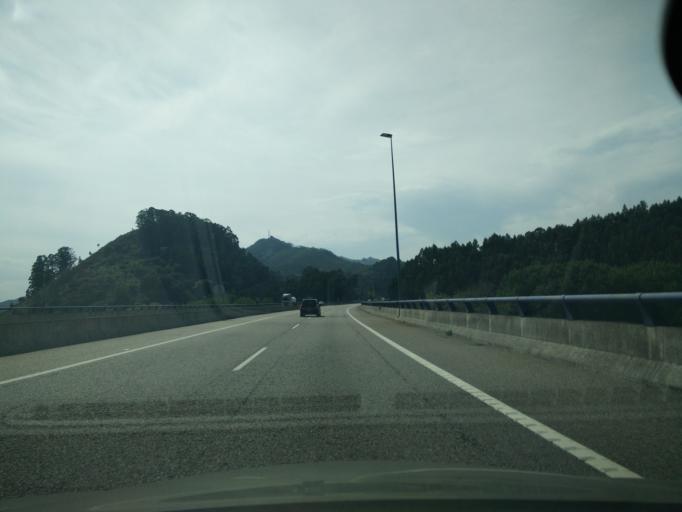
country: ES
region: Asturias
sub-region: Province of Asturias
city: Ribadesella
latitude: 43.4351
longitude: -5.0585
